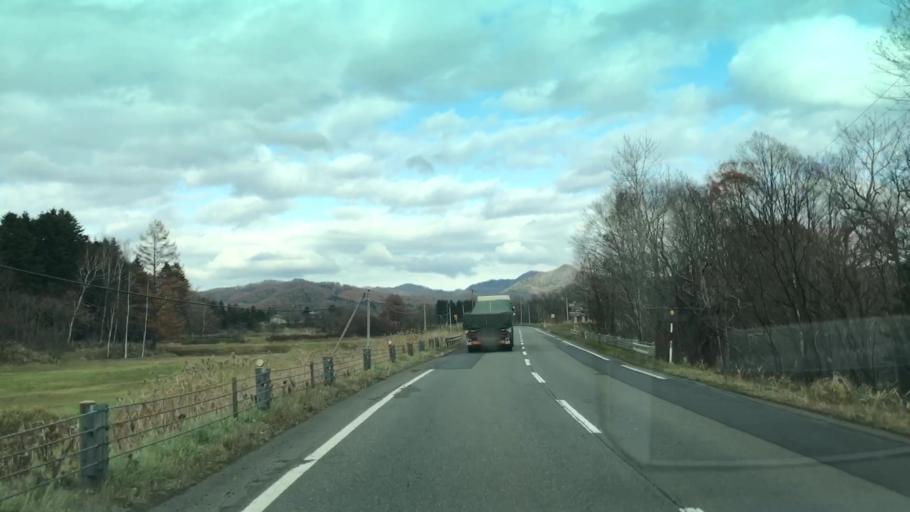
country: JP
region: Hokkaido
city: Shimo-furano
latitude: 42.8660
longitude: 142.4243
